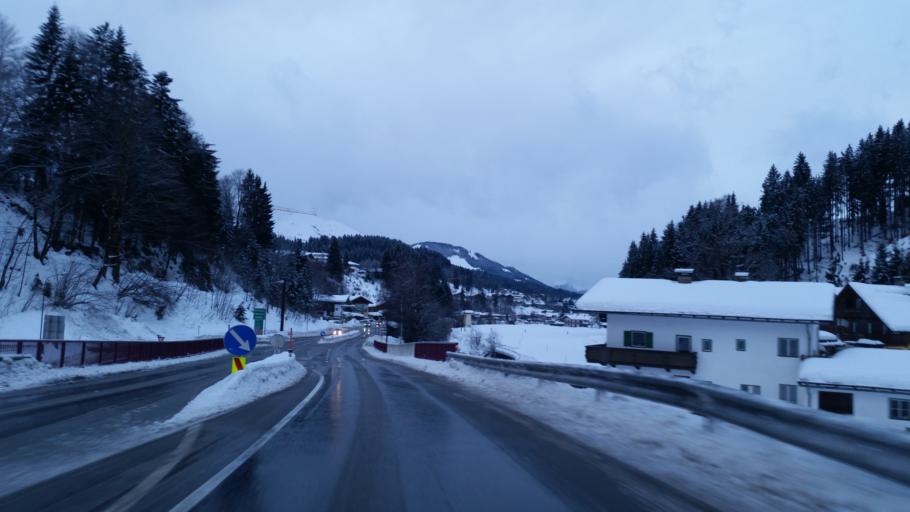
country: AT
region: Tyrol
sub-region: Politischer Bezirk Kitzbuhel
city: Fieberbrunn
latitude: 47.4727
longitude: 12.5574
